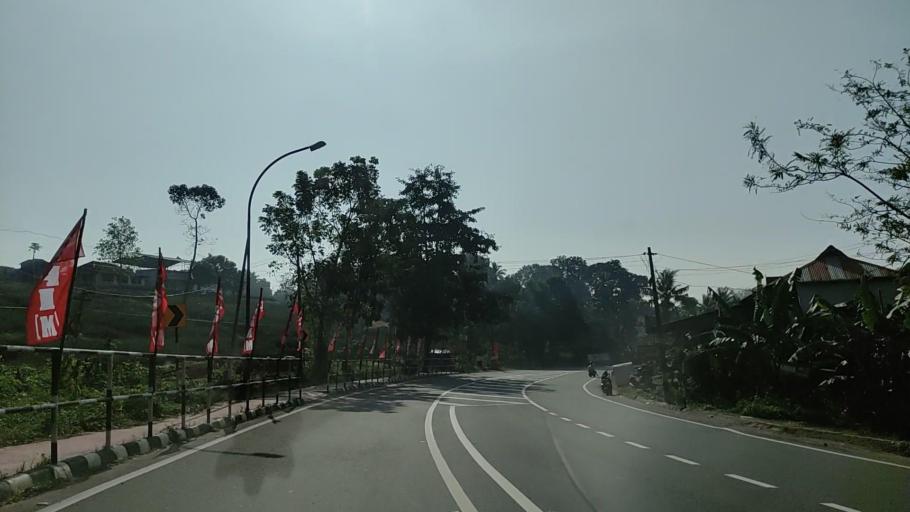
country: IN
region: Kerala
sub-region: Kollam
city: Punalur
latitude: 8.9628
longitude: 76.8368
